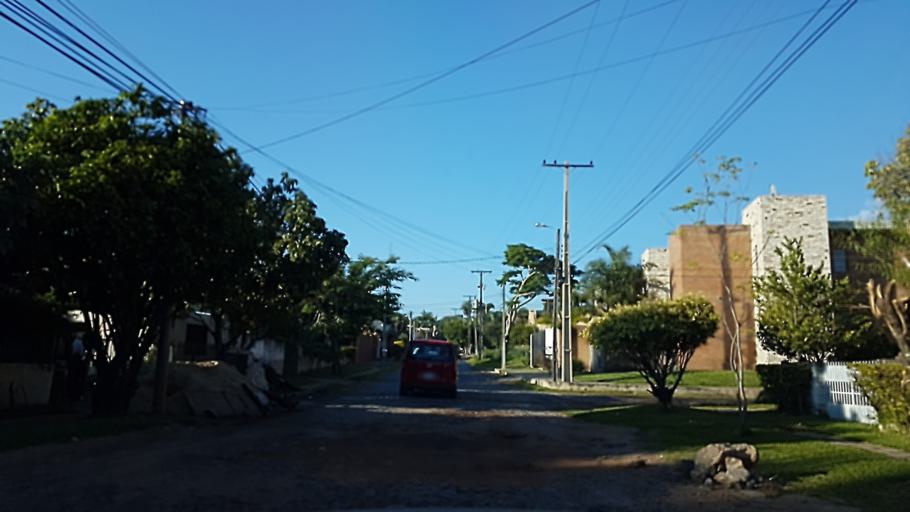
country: PY
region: Central
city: Fernando de la Mora
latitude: -25.2653
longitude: -57.5501
